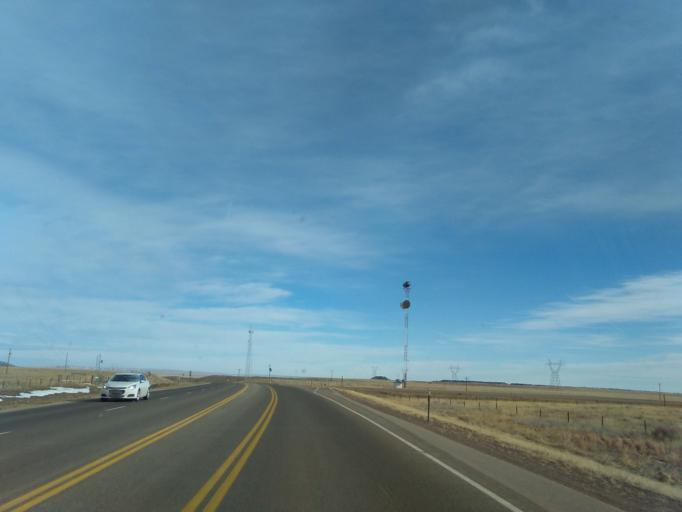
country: US
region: Wyoming
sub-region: Laramie County
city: Pine Bluffs
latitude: 41.4407
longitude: -104.3474
